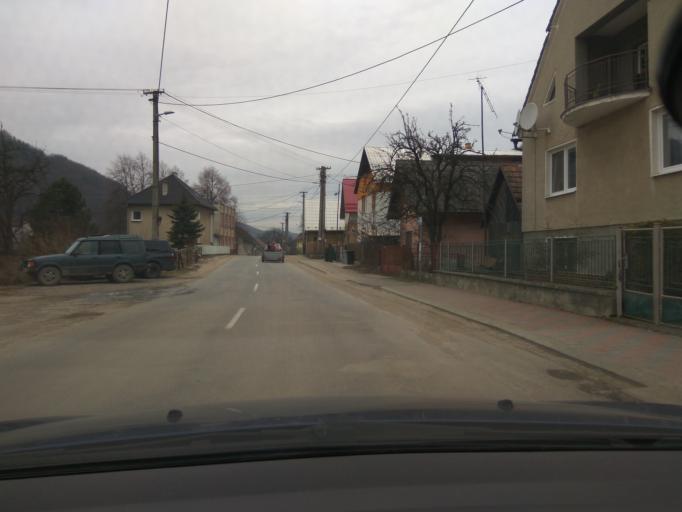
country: SK
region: Nitriansky
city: Ilava
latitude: 48.9782
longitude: 18.3167
